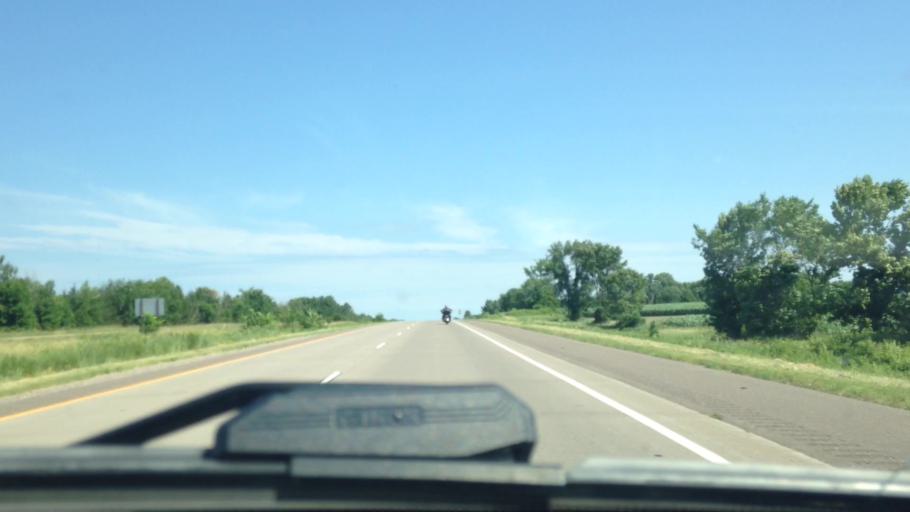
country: US
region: Wisconsin
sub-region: Barron County
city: Rice Lake
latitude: 45.4830
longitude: -91.7612
